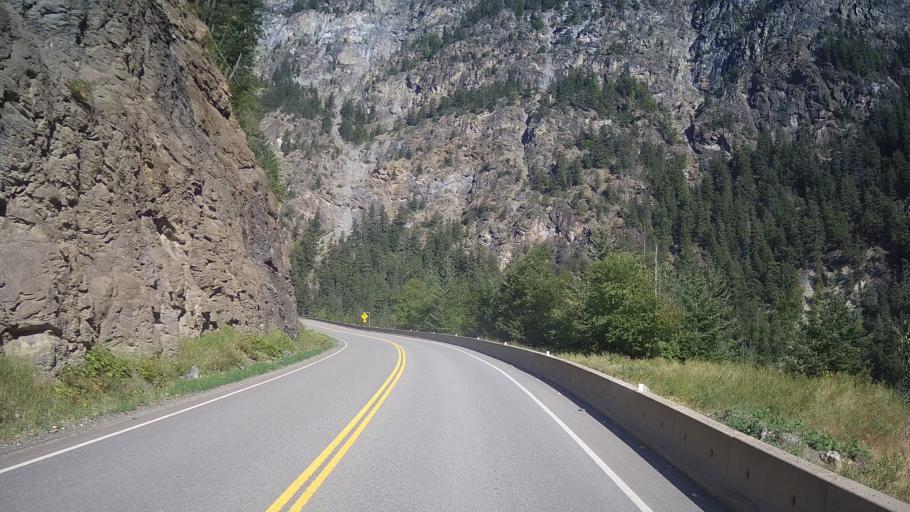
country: CA
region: British Columbia
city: Lillooet
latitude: 50.6462
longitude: -122.0661
